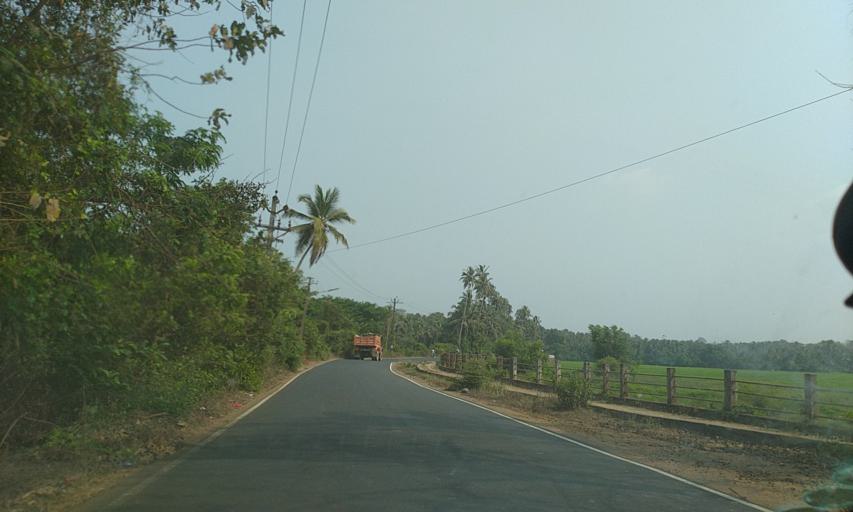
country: IN
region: Goa
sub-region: South Goa
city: Quepem
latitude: 15.2591
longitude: 74.0483
